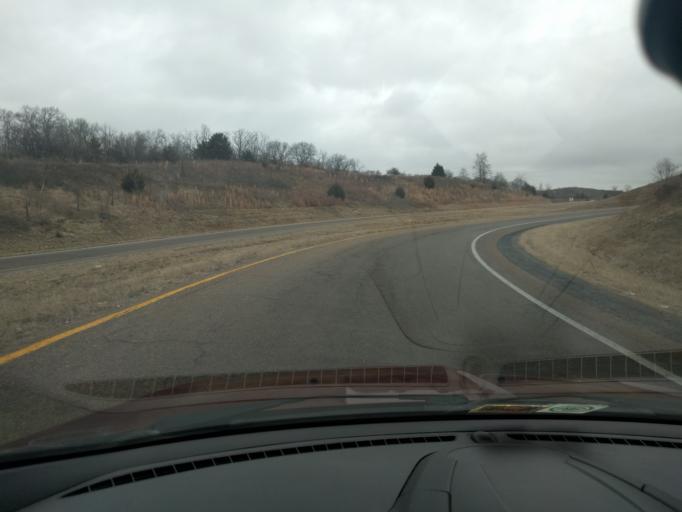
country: US
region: Virginia
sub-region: Augusta County
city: Jolivue
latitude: 38.1201
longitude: -79.0684
